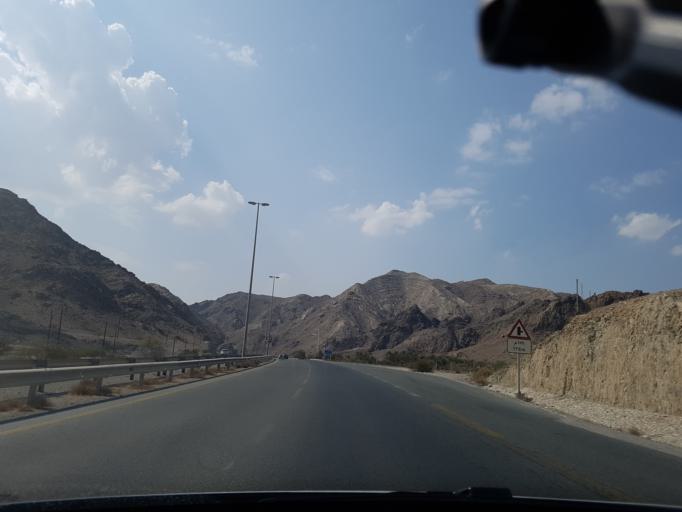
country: AE
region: Al Fujayrah
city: Dibba Al-Fujairah
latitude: 25.5333
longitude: 56.1330
